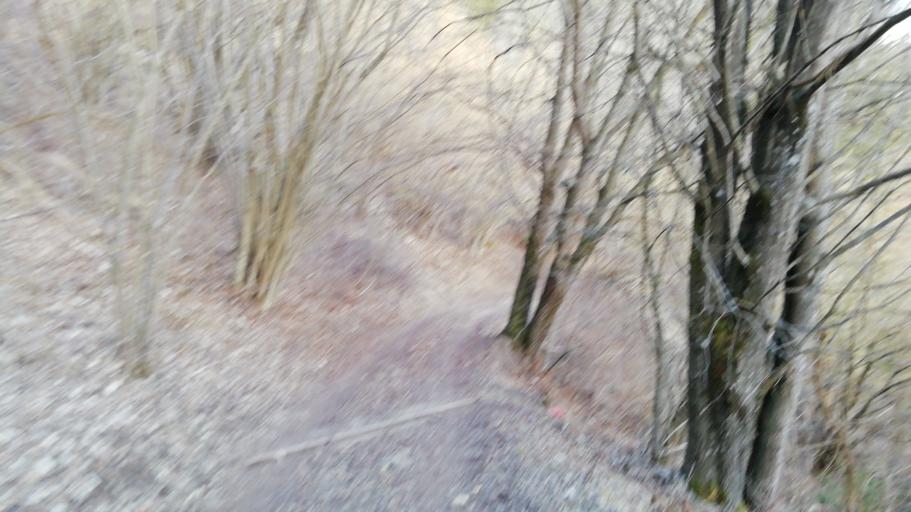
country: IT
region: Veneto
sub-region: Provincia di Belluno
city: Valle di Cadore
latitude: 46.4215
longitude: 12.3157
